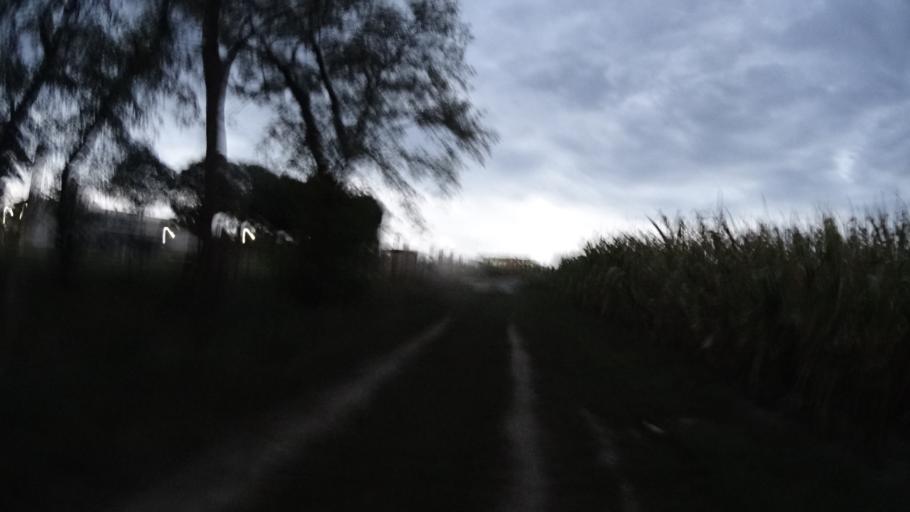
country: PL
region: Masovian Voivodeship
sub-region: Powiat warszawski zachodni
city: Babice
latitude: 52.2279
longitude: 20.8573
